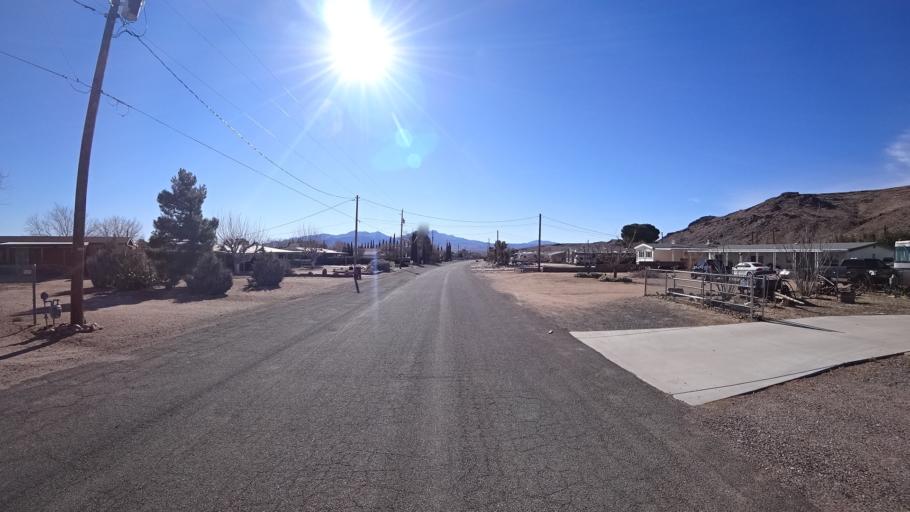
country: US
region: Arizona
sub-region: Mohave County
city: New Kingman-Butler
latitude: 35.2695
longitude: -114.0473
